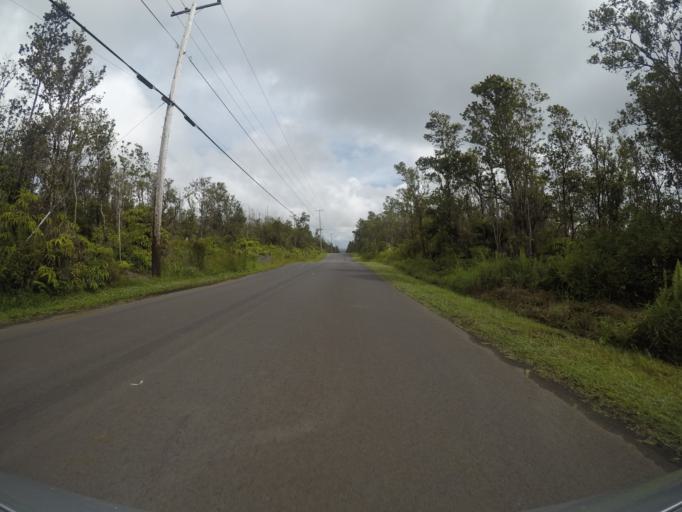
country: US
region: Hawaii
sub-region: Hawaii County
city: Fern Acres
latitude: 19.4673
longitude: -155.1353
